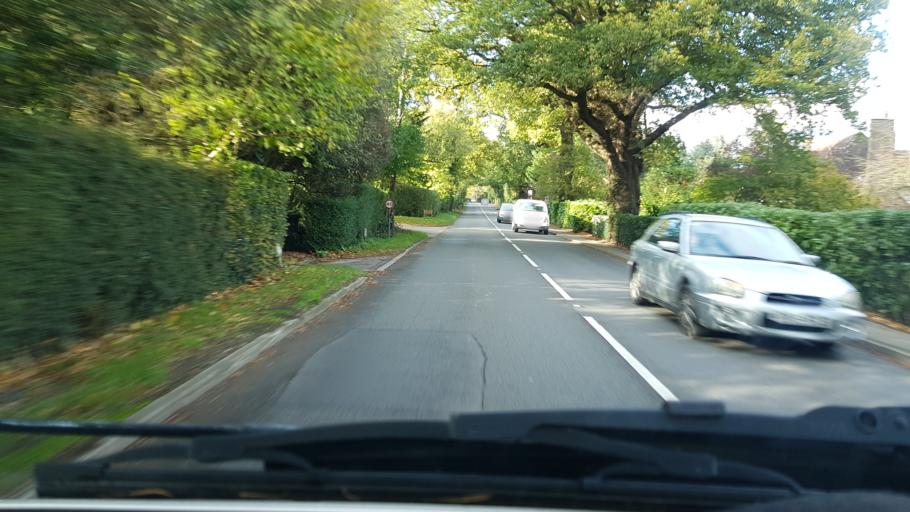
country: GB
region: England
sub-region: Surrey
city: Send
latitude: 51.2698
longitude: -0.5059
